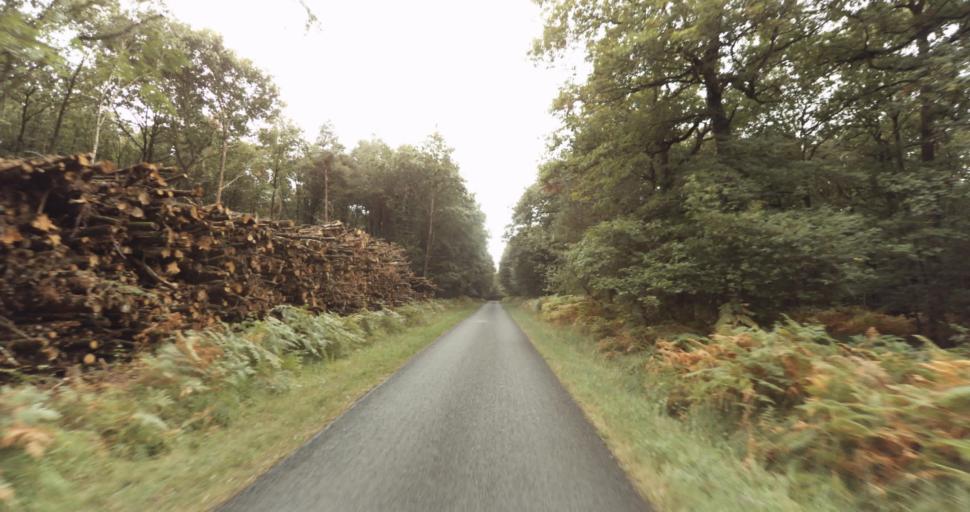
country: FR
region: Lower Normandy
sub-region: Departement de l'Orne
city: Sainte-Gauburge-Sainte-Colombe
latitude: 48.7555
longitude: 0.4741
